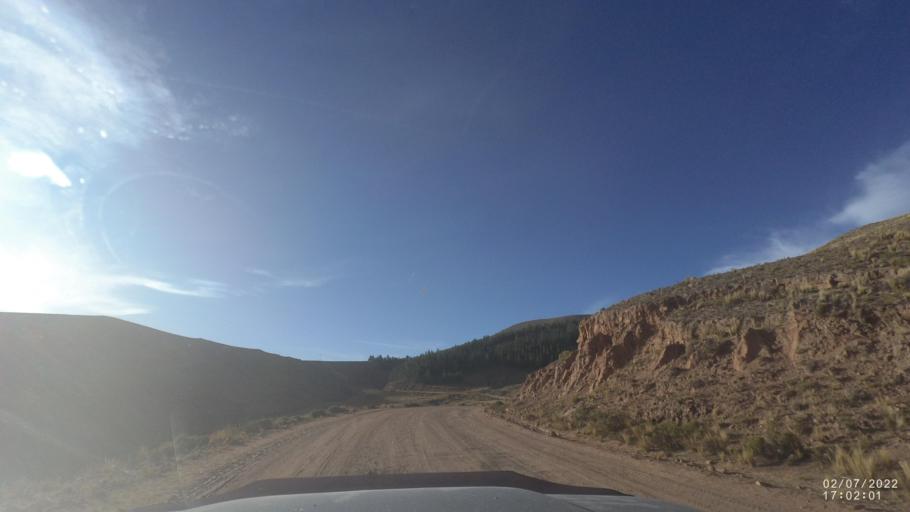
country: BO
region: Cochabamba
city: Irpa Irpa
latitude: -17.9287
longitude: -66.5543
